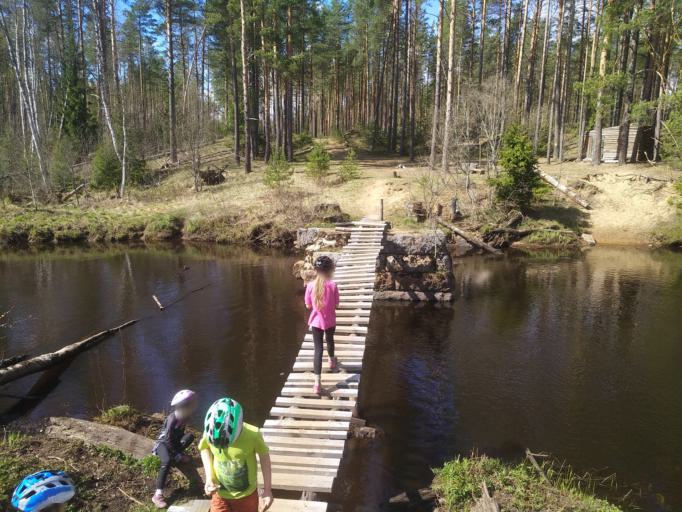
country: RU
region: Leningrad
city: Sosnovo
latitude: 60.5950
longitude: 30.1668
